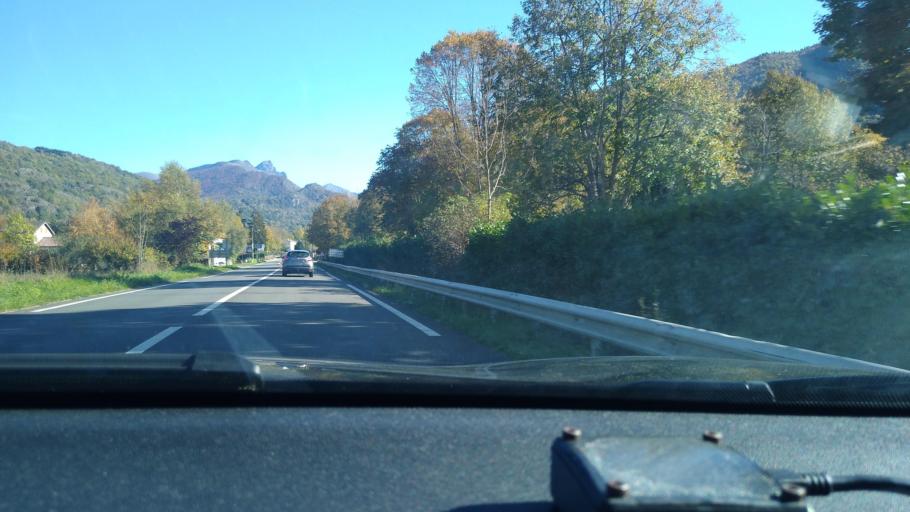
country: FR
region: Midi-Pyrenees
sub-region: Departement de l'Ariege
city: Ax-les-Thermes
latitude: 42.7308
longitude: 1.8116
